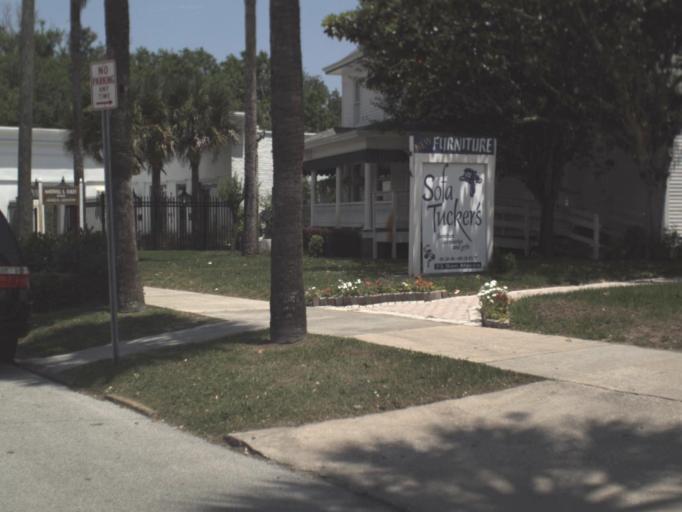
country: US
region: Florida
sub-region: Saint Johns County
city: Saint Augustine
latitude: 29.9020
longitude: -81.3160
